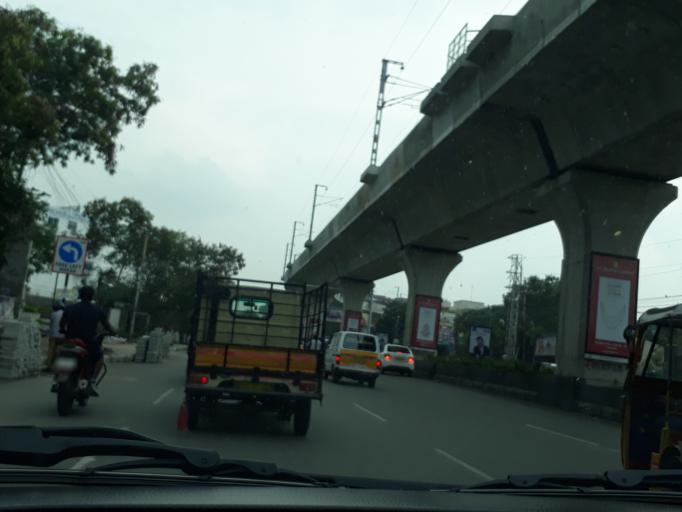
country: IN
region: Telangana
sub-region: Rangareddi
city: Kukatpalli
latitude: 17.4280
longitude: 78.4171
